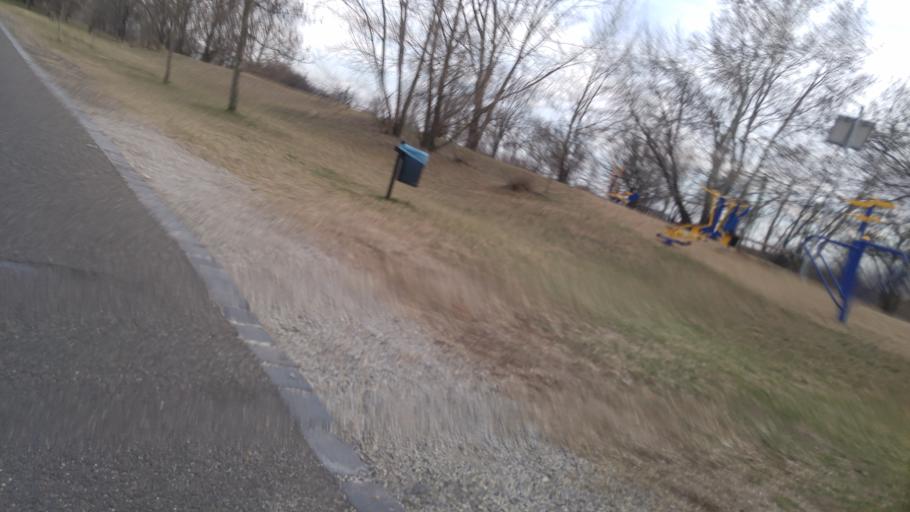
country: HU
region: Budapest
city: Budapest XVII. keruelet
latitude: 47.4735
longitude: 19.2305
